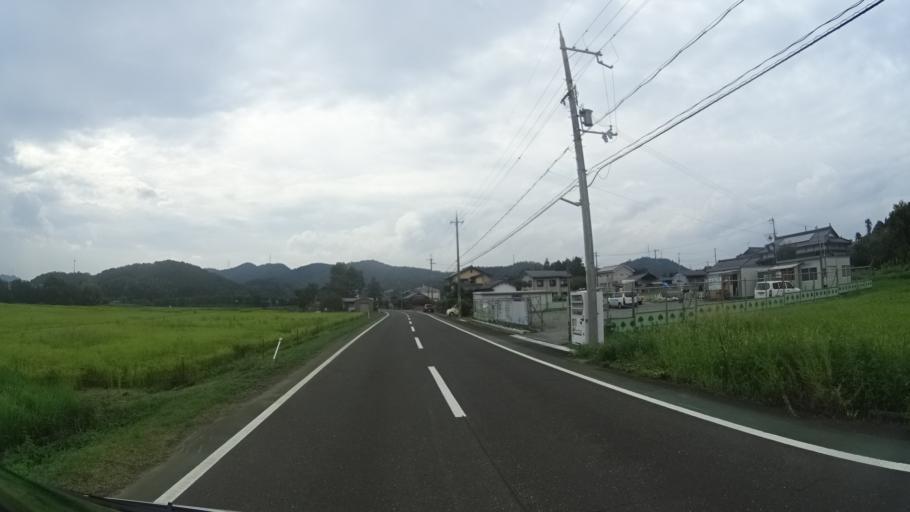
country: JP
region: Kyoto
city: Ayabe
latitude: 35.3580
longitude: 135.3217
